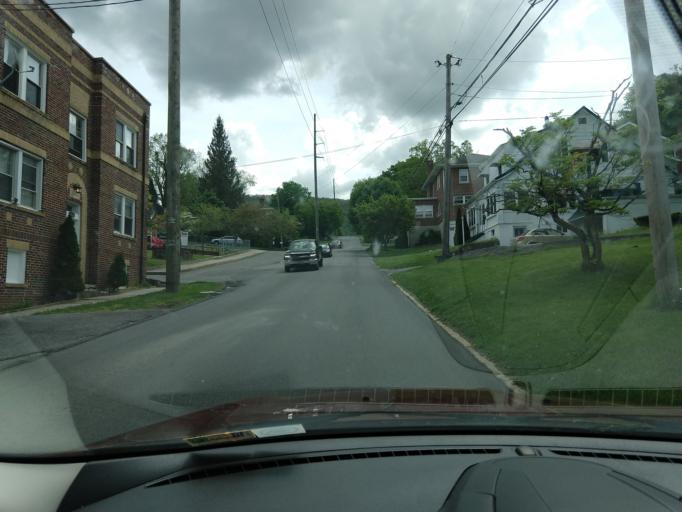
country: US
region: West Virginia
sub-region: Mercer County
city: Bluefield
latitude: 37.2501
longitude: -81.2314
